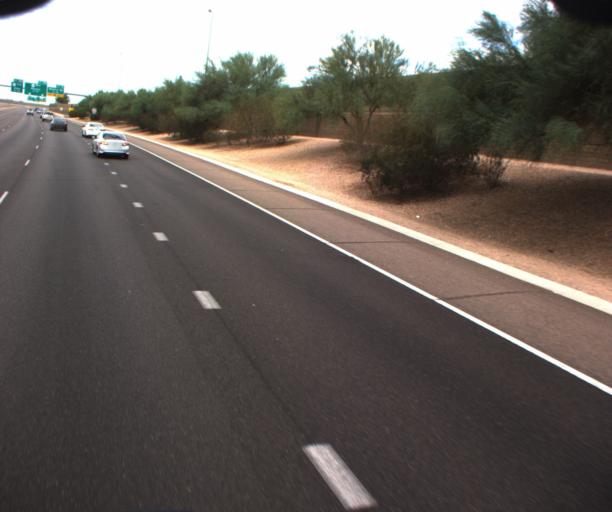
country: US
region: Arizona
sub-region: Pinal County
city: Apache Junction
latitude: 33.3693
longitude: -111.6448
